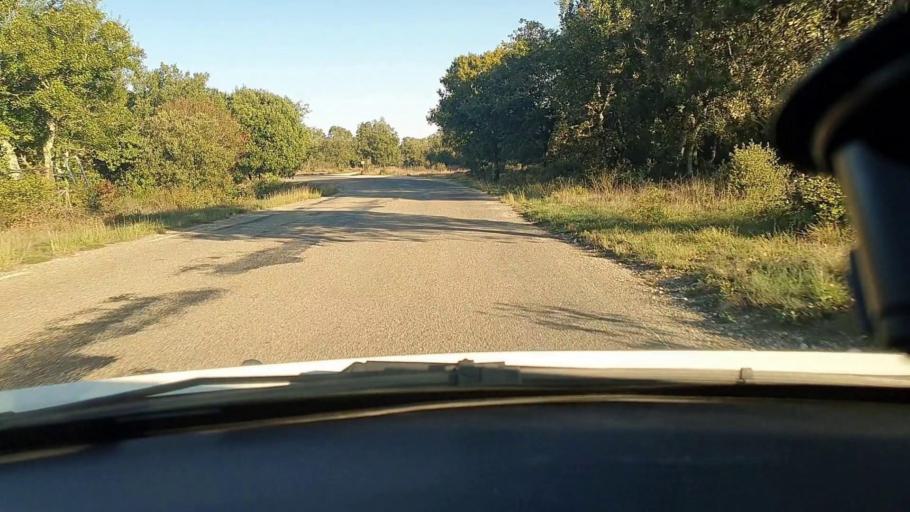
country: FR
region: Languedoc-Roussillon
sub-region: Departement du Gard
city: Barjac
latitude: 44.2229
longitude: 4.3339
